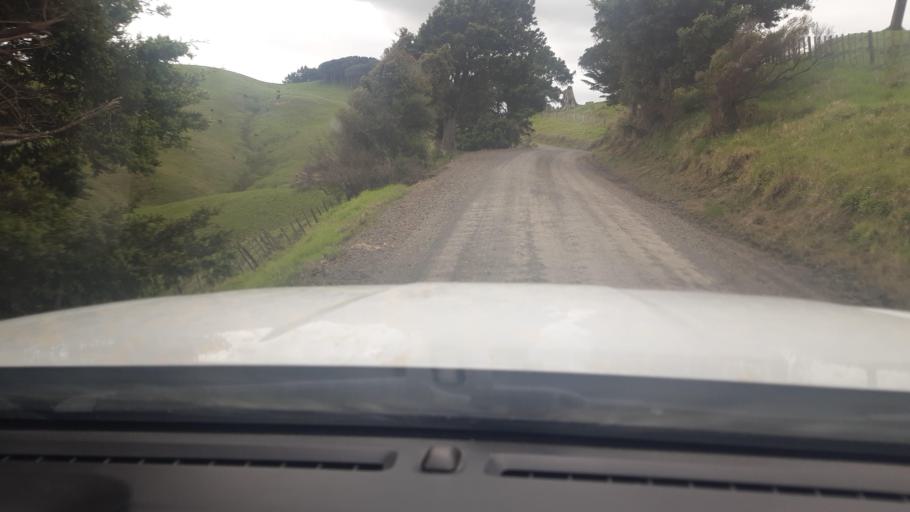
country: NZ
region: Northland
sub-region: Far North District
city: Kaitaia
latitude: -35.0850
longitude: 173.3220
